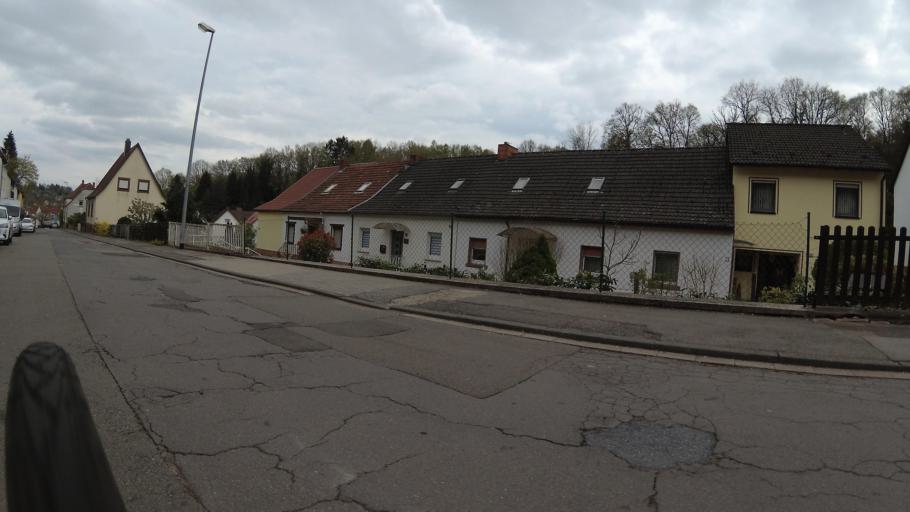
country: DE
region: Rheinland-Pfalz
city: Zweibrucken
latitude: 49.2327
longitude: 7.3494
